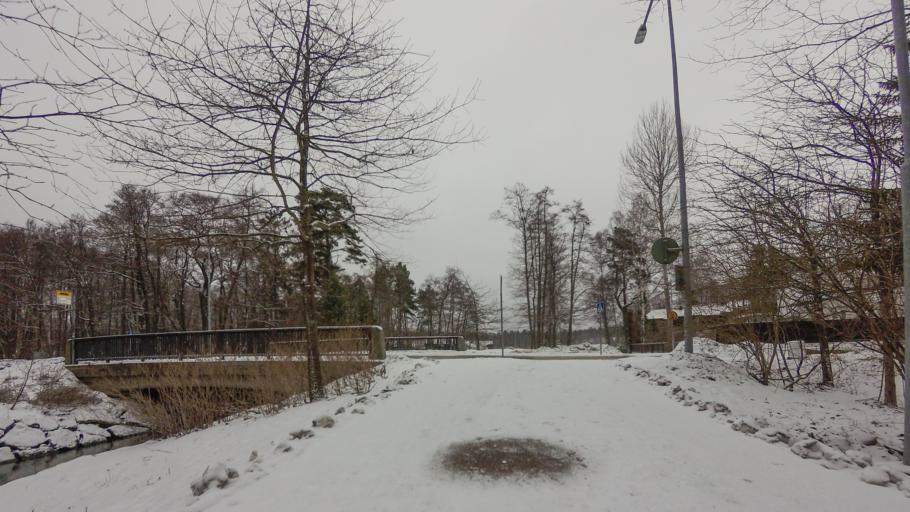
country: FI
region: Uusimaa
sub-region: Helsinki
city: Vantaa
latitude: 60.1954
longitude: 25.0640
